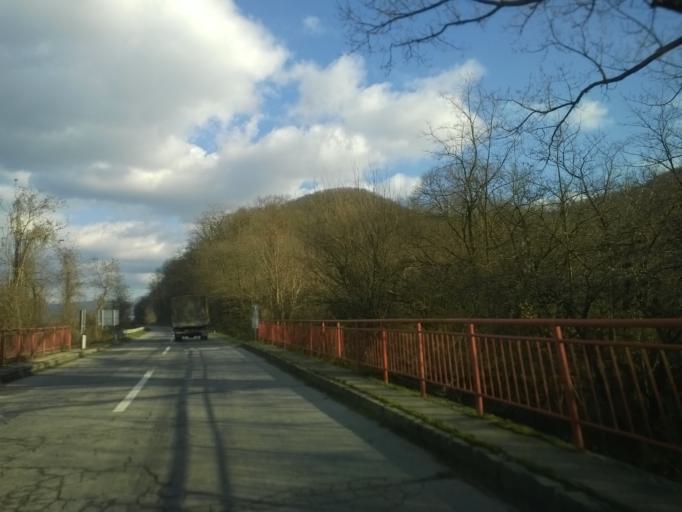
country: RO
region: Caras-Severin
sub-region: Comuna Berzasca
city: Liubcova
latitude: 44.6461
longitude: 21.8406
